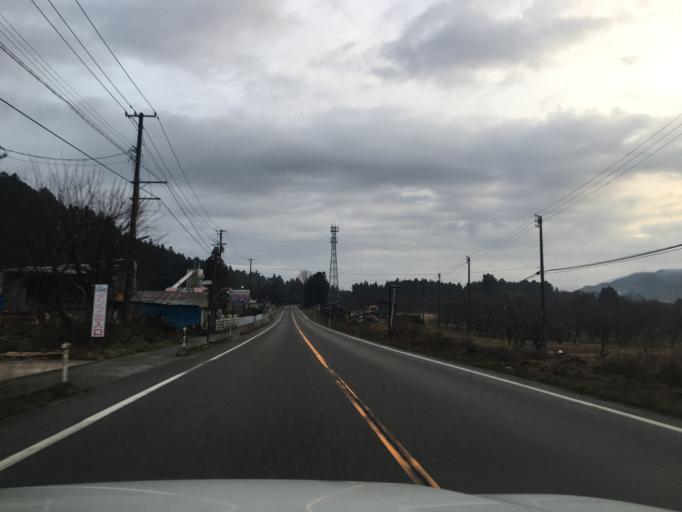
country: JP
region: Niigata
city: Murakami
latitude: 38.2895
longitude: 139.5265
